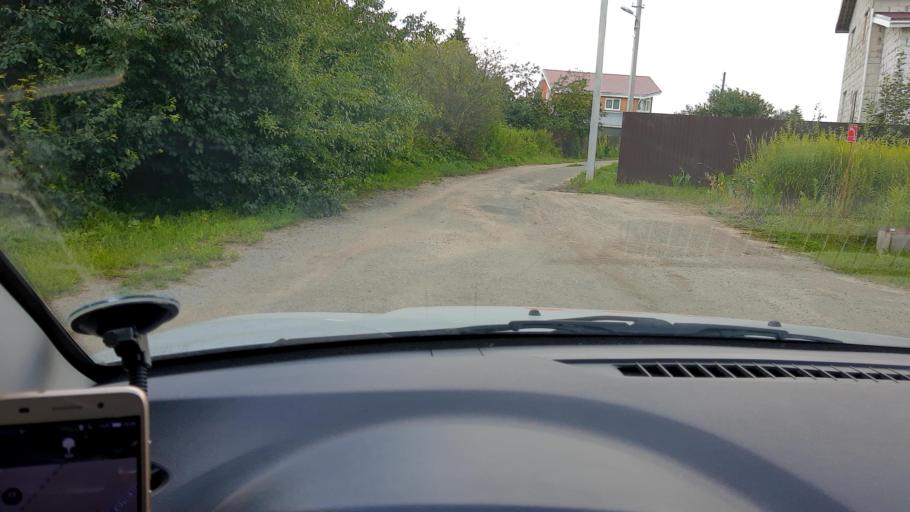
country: RU
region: Nizjnij Novgorod
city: Afonino
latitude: 56.2005
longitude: 44.0300
